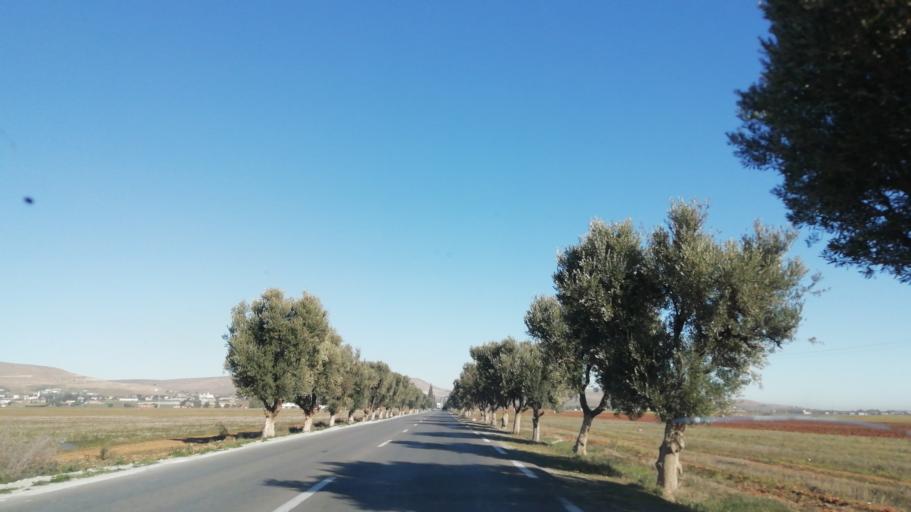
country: DZ
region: Mascara
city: Mascara
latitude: 35.2079
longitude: 0.1103
